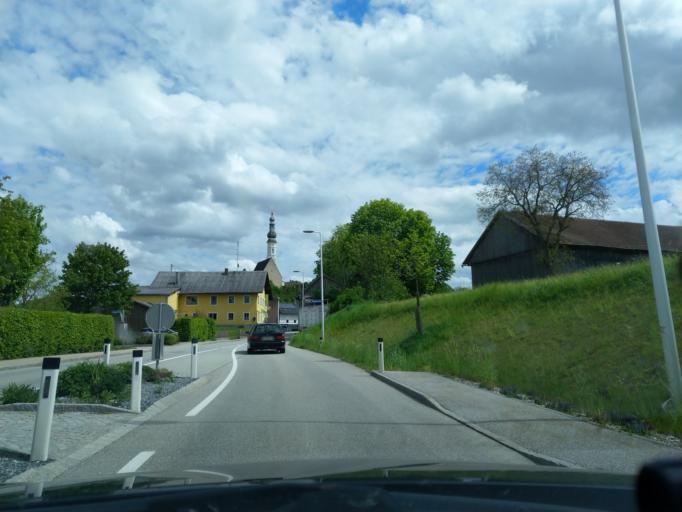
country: AT
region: Upper Austria
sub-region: Politischer Bezirk Braunau am Inn
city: Altheim
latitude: 48.2647
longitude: 13.2903
